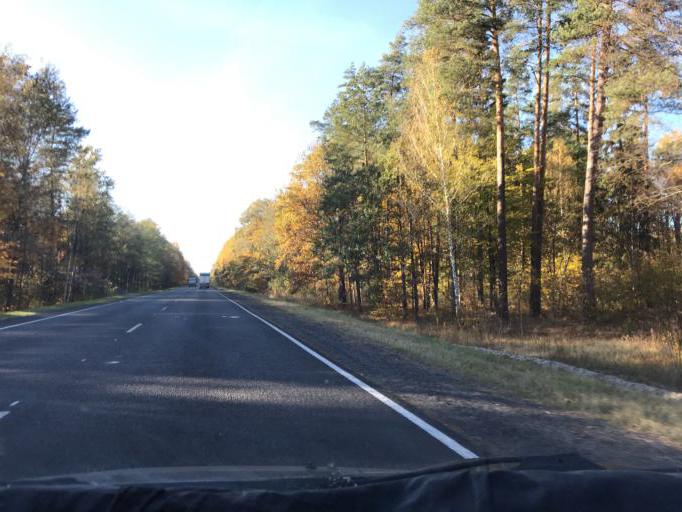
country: BY
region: Gomel
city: Mazyr
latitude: 52.1809
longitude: 29.1641
